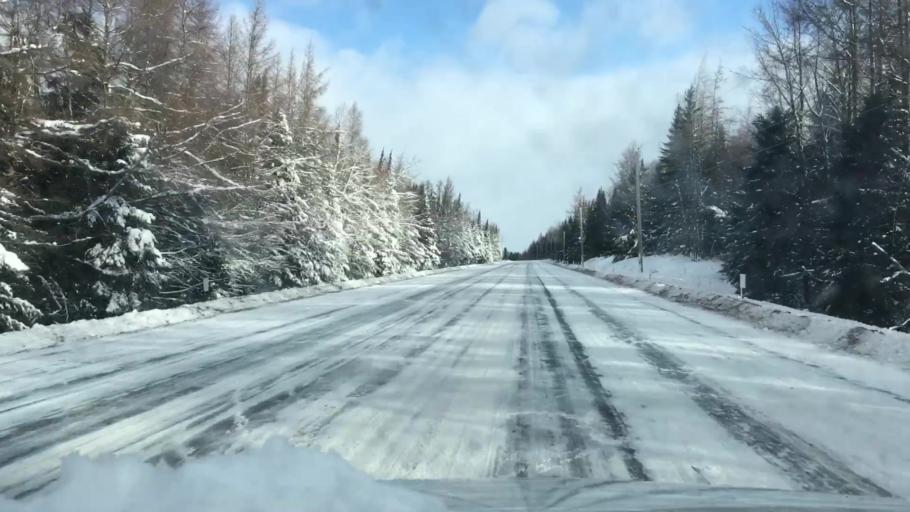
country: US
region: Maine
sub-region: Aroostook County
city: Van Buren
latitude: 47.0620
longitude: -67.9904
